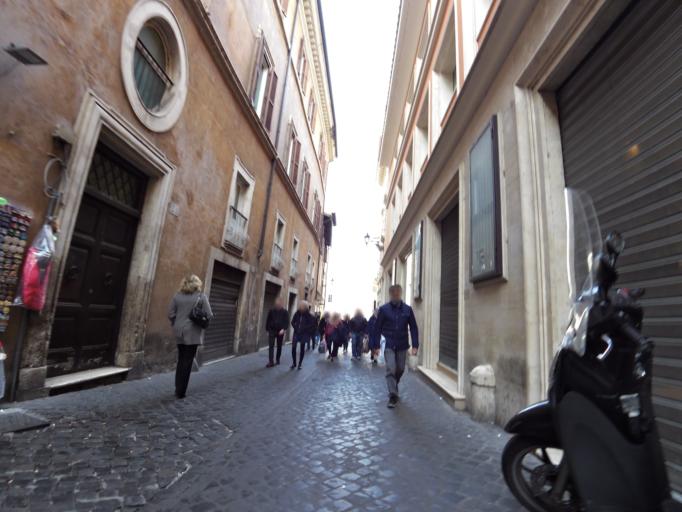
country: IT
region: Latium
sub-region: Citta metropolitana di Roma Capitale
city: Rome
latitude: 41.9003
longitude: 12.4838
